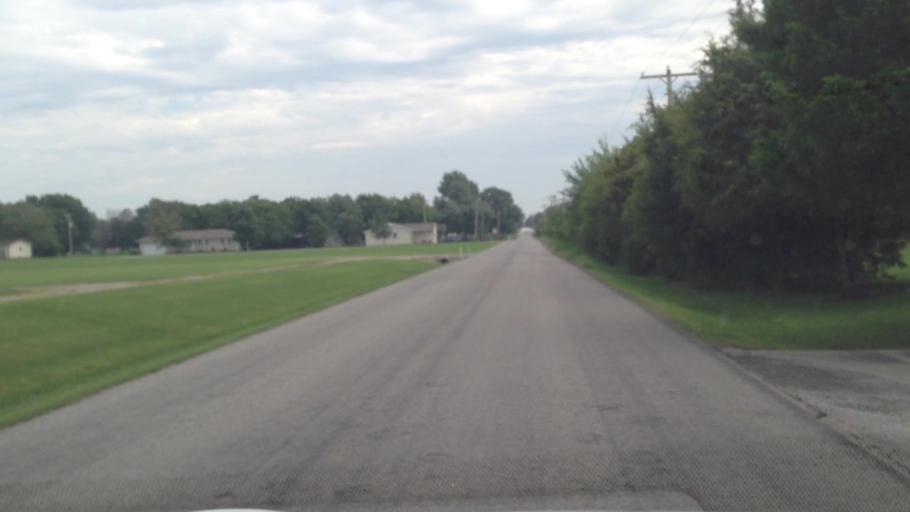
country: US
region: Kansas
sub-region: Crawford County
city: Girard
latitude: 37.4992
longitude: -94.8492
